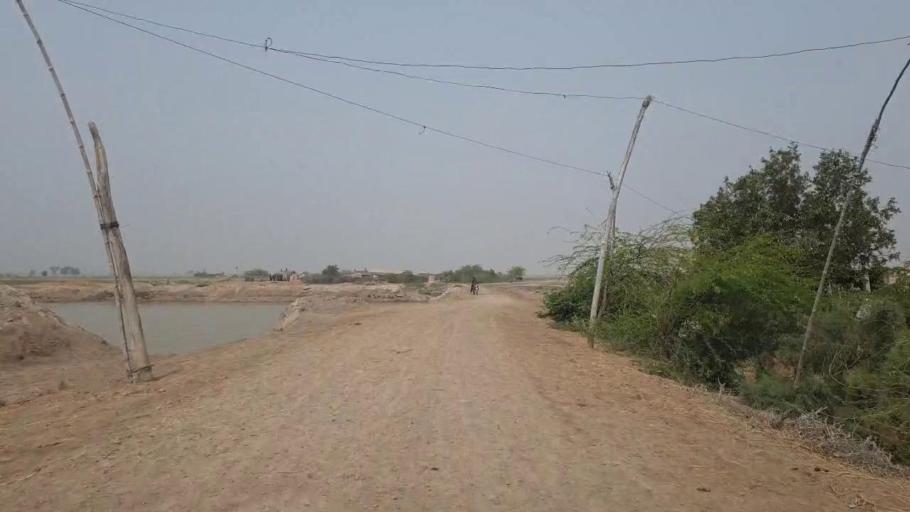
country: PK
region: Sindh
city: Kario
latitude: 24.6619
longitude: 68.6389
